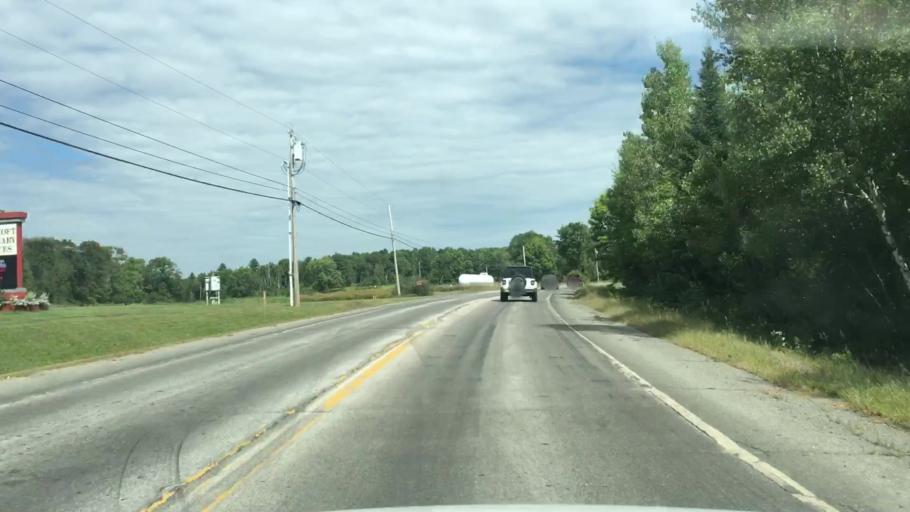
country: US
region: Maine
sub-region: Piscataquis County
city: Dover-Foxcroft
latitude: 45.1535
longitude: -69.2358
